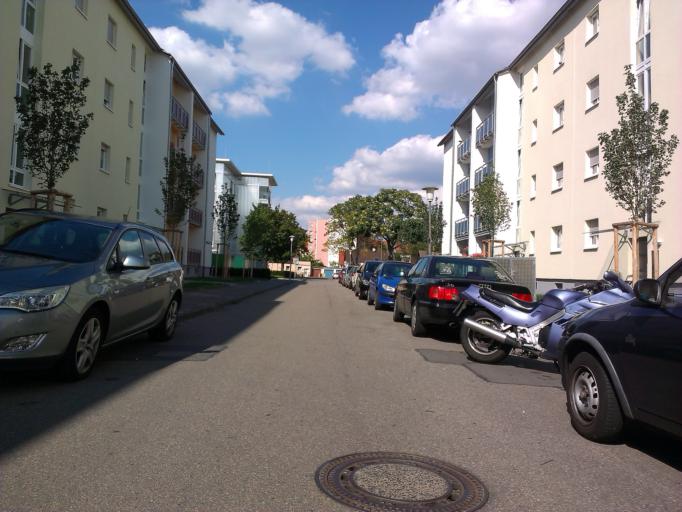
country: DE
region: Baden-Wuerttemberg
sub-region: Karlsruhe Region
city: Mannheim
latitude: 49.5458
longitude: 8.4757
